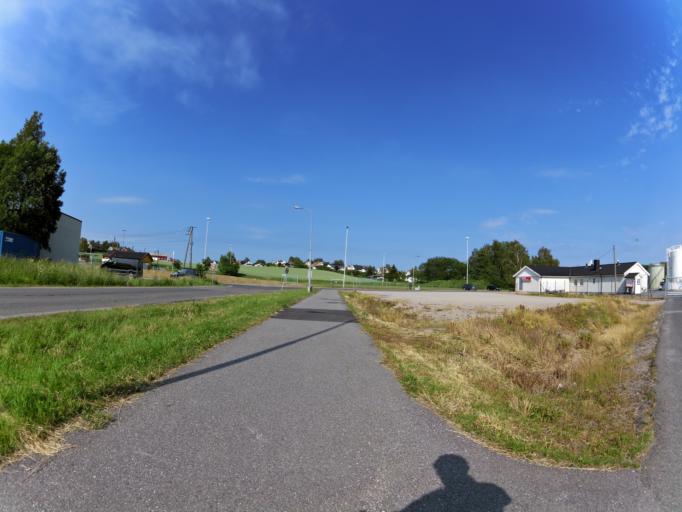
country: NO
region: Ostfold
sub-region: Fredrikstad
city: Fredrikstad
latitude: 59.2411
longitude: 10.9965
